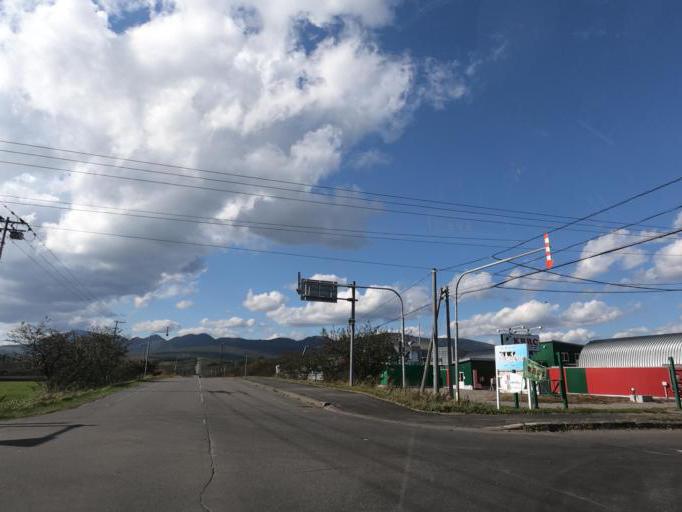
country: JP
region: Hokkaido
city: Otofuke
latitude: 43.2427
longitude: 143.2493
